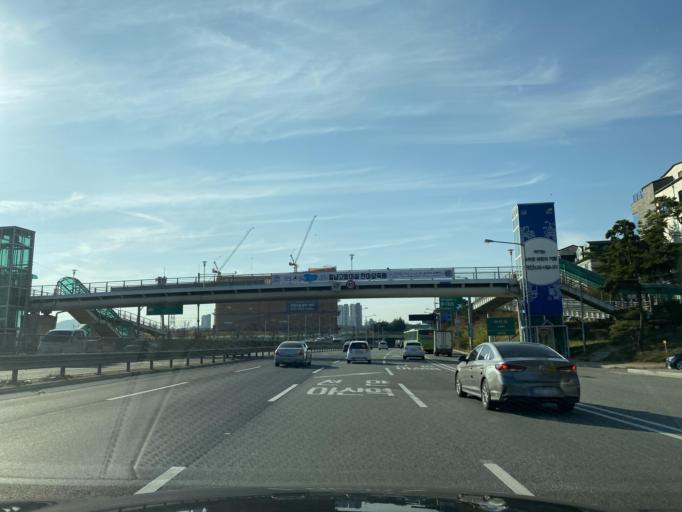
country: KR
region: Chungcheongnam-do
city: Cheonan
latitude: 36.7847
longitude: 127.1138
